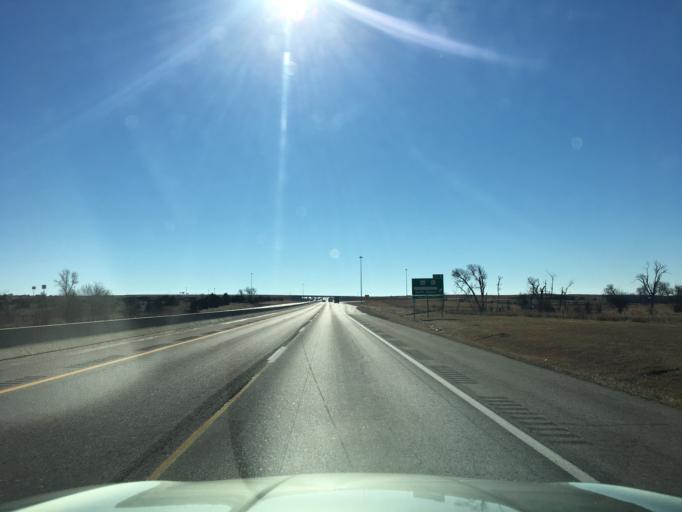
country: US
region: Kansas
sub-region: Sumner County
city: Wellington
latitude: 37.0640
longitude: -97.3385
